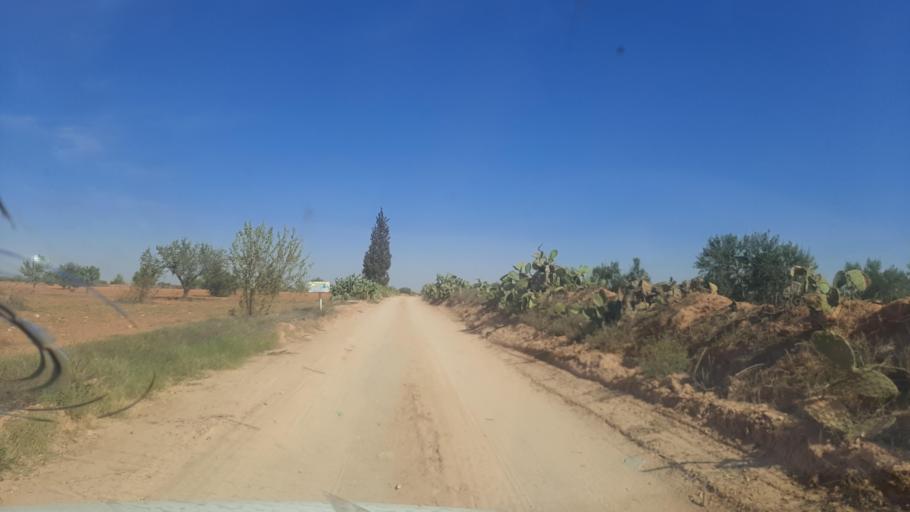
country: TN
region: Safaqis
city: Sfax
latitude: 34.8796
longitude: 10.5737
